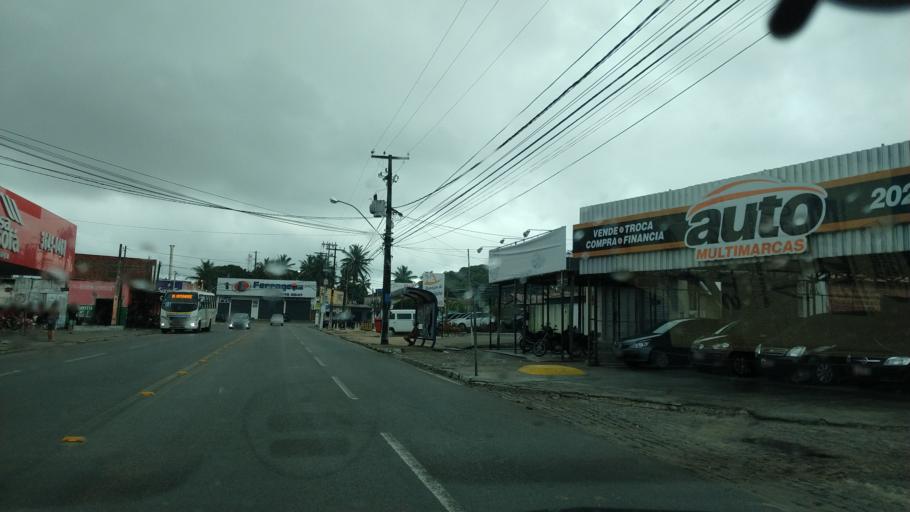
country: BR
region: Rio Grande do Norte
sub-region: Parnamirim
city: Parnamirim
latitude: -5.9267
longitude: -35.2700
